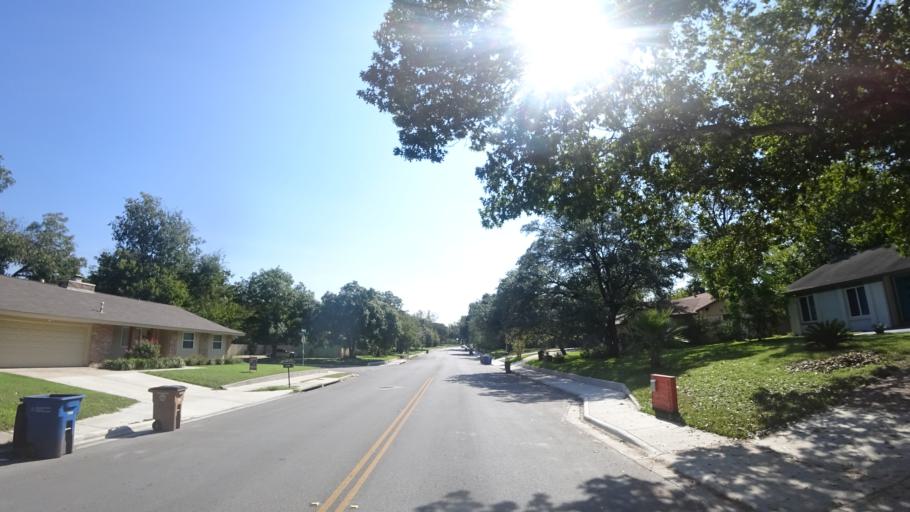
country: US
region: Texas
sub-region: Travis County
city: Austin
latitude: 30.3119
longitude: -97.6698
